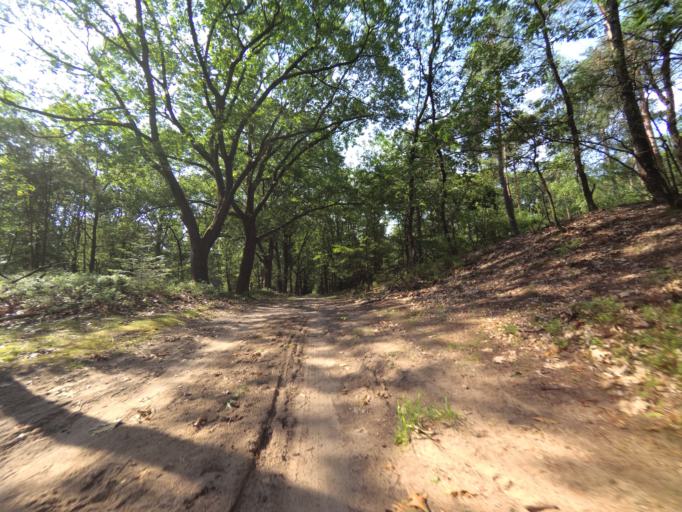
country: NL
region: Gelderland
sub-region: Gemeente Apeldoorn
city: Beekbergen
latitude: 52.1361
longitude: 5.9391
